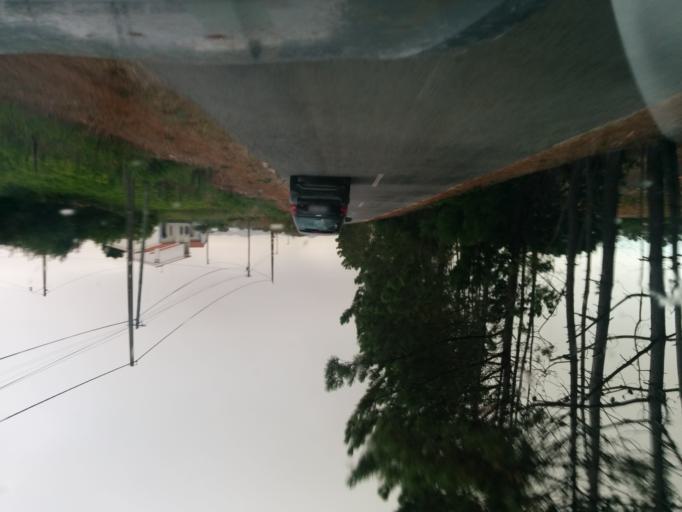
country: PT
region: Beja
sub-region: Odemira
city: Vila Nova de Milfontes
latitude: 37.6080
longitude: -8.7972
